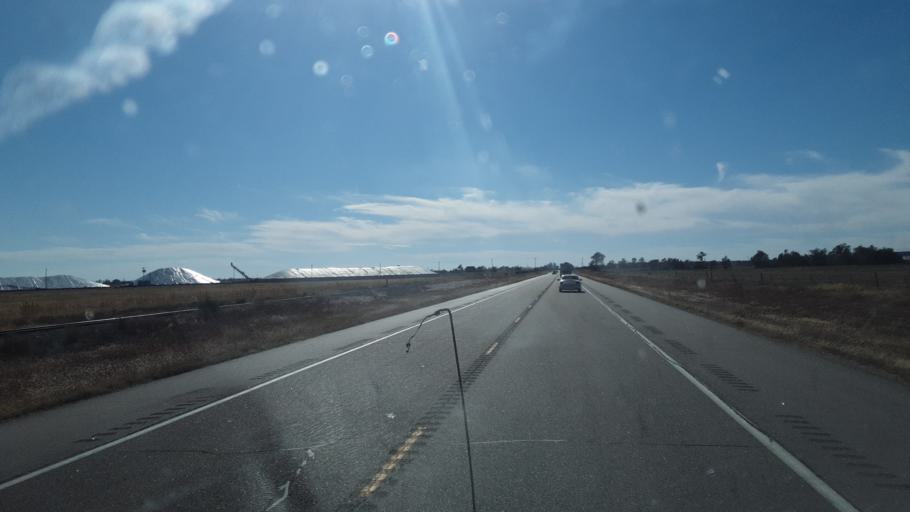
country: US
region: Kansas
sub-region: Pawnee County
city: Larned
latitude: 38.2071
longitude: -99.0614
